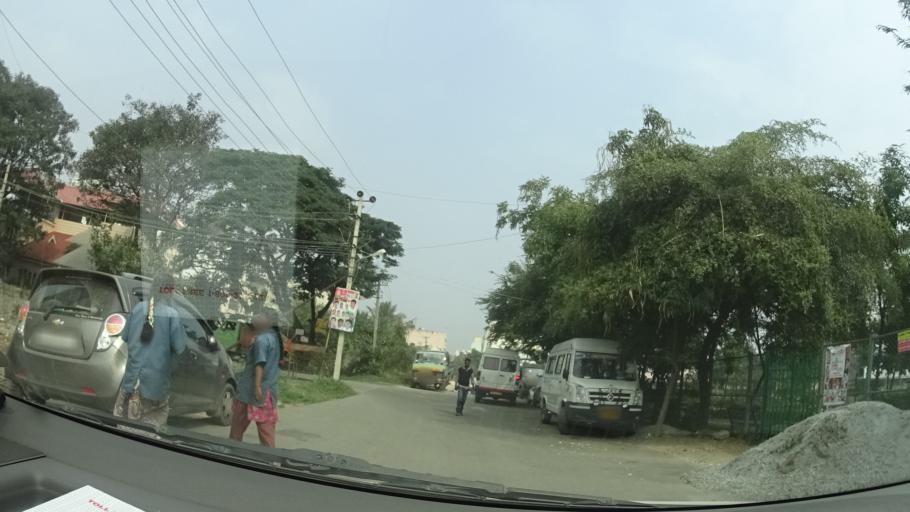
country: IN
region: Karnataka
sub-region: Bangalore Urban
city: Bangalore
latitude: 13.0264
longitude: 77.6250
